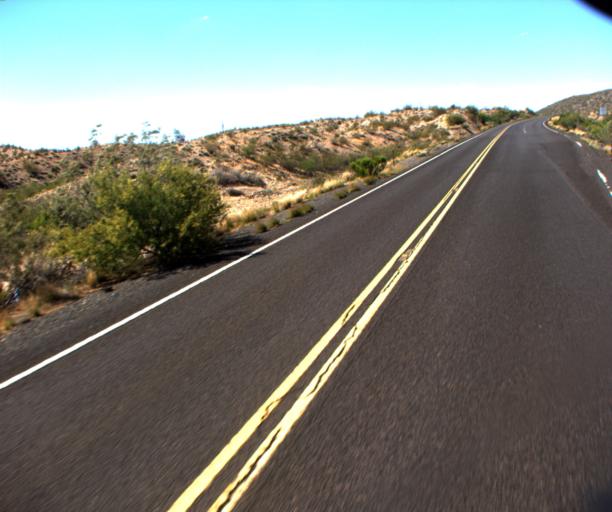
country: US
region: Arizona
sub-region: Mohave County
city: Kingman
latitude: 34.9237
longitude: -113.6583
